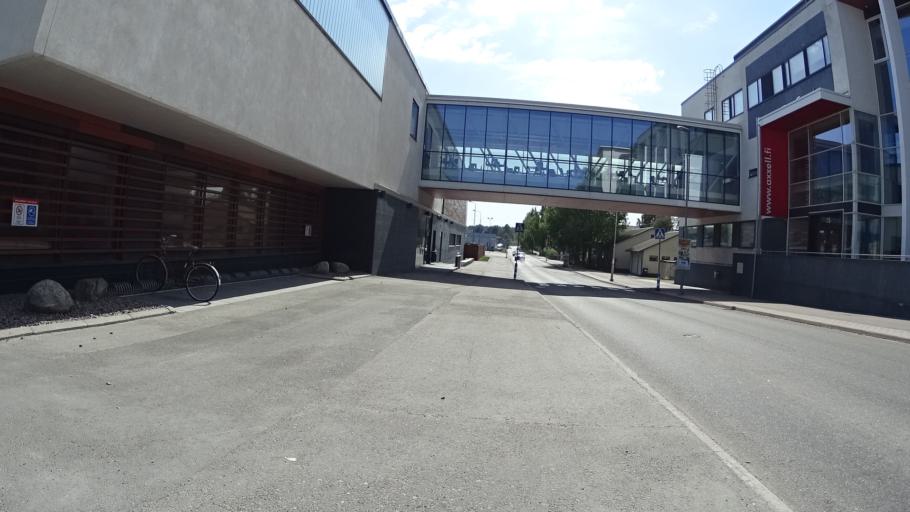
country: FI
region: Uusimaa
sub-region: Raaseporin
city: Karis
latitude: 60.0690
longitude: 23.6595
